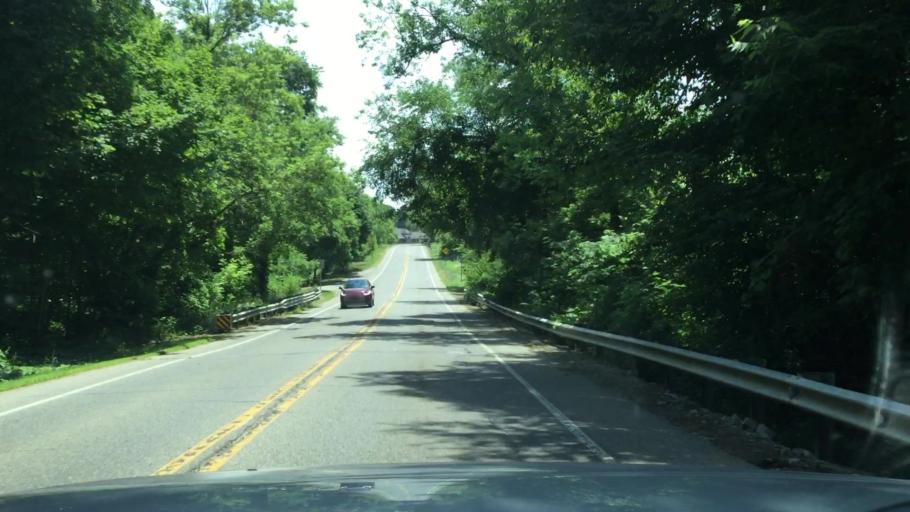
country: US
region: Michigan
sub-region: Genesee County
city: Flushing
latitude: 43.0660
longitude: -83.8657
